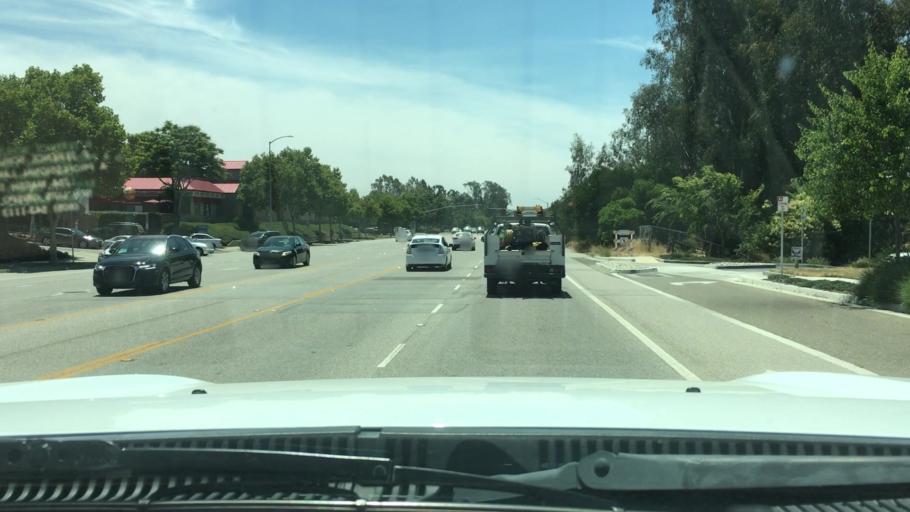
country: US
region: California
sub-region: San Luis Obispo County
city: San Luis Obispo
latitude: 35.2503
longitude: -120.6443
